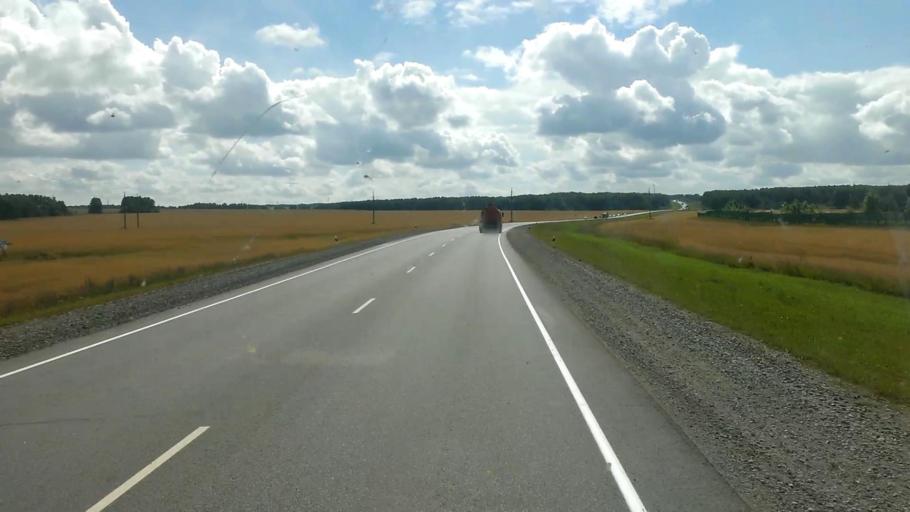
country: RU
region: Altai Krai
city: Troitskoye
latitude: 52.9937
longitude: 84.7407
